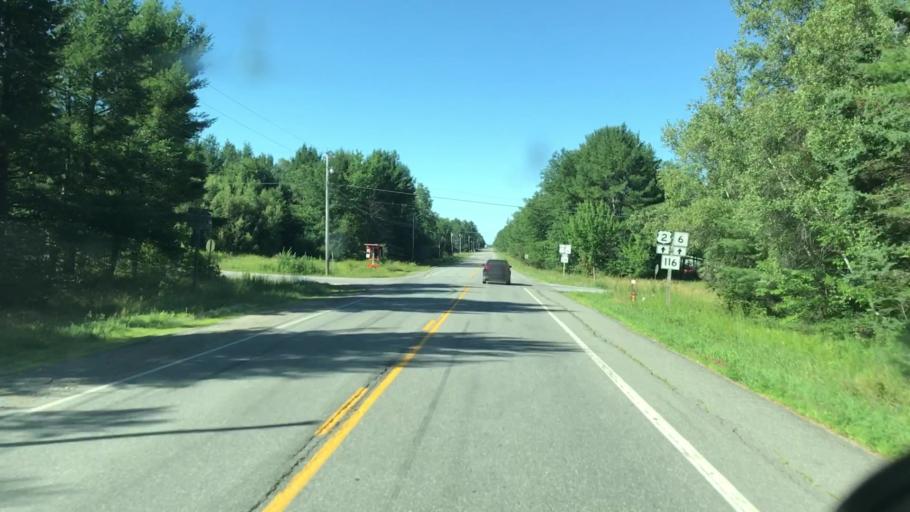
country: US
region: Maine
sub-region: Penobscot County
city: Enfield
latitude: 45.3240
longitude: -68.5958
